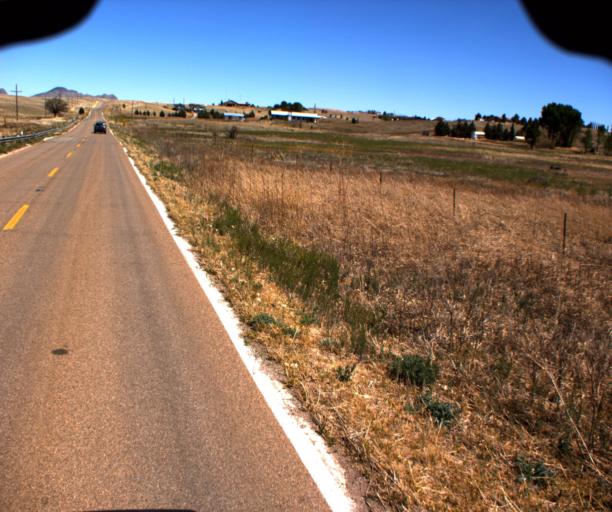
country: US
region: Arizona
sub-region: Cochise County
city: Huachuca City
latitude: 31.6735
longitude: -110.6172
